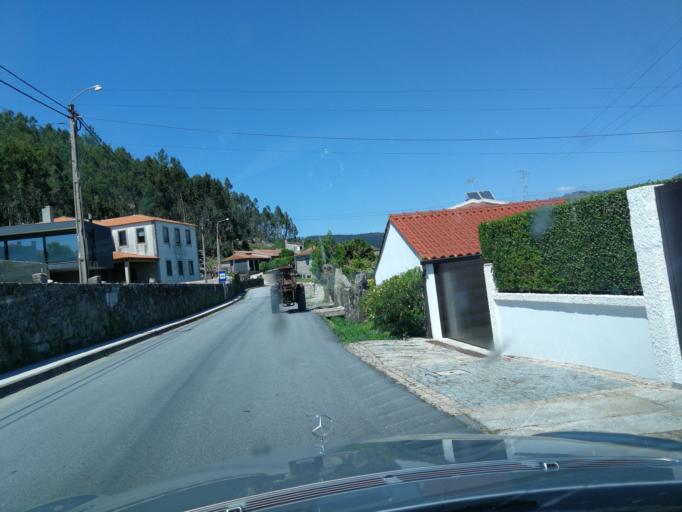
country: PT
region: Viana do Castelo
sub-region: Viana do Castelo
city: Meadela
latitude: 41.7405
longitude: -8.7827
